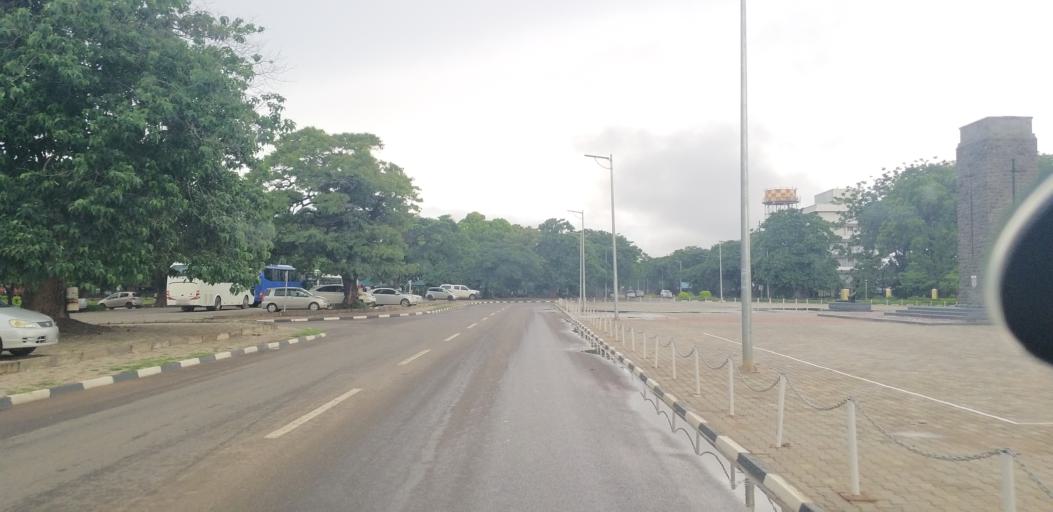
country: ZM
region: Lusaka
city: Lusaka
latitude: -15.4221
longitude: 28.3086
